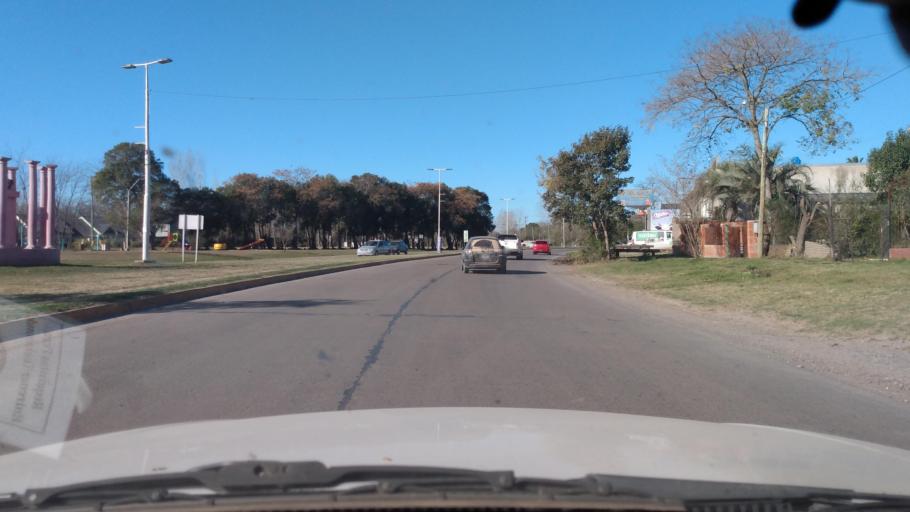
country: AR
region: Buenos Aires
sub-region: Partido de Mercedes
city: Mercedes
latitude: -34.6479
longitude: -59.4159
